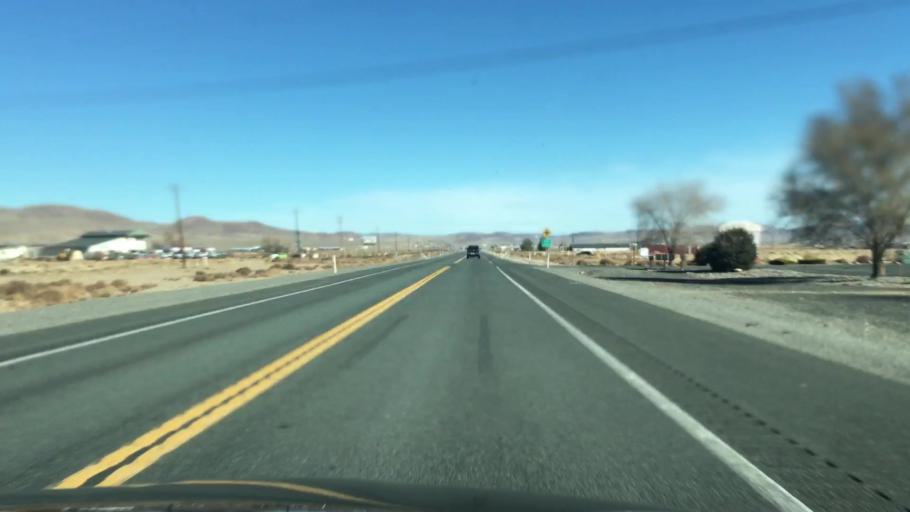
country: US
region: Nevada
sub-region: Lyon County
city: Silver Springs
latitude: 39.3959
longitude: -119.2801
